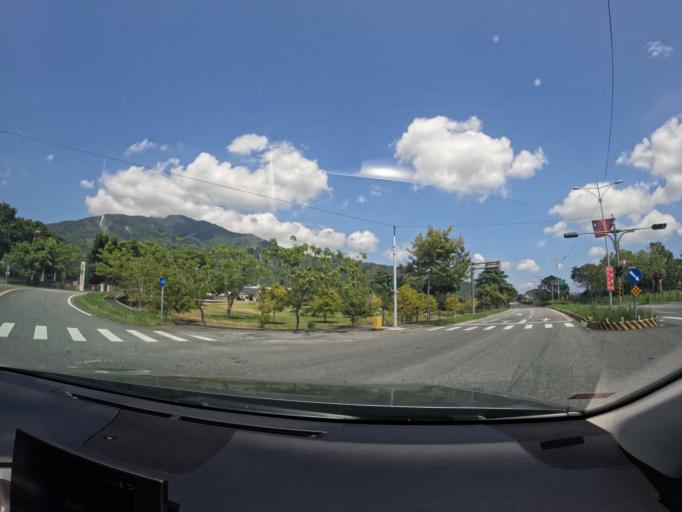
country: TW
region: Taiwan
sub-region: Hualien
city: Hualian
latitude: 23.7077
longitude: 121.4193
